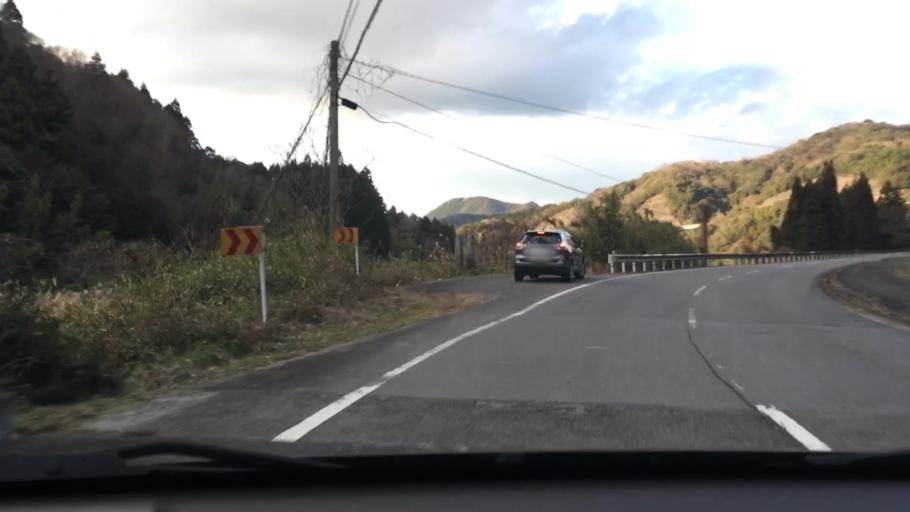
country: JP
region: Oita
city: Hiji
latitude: 33.4263
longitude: 131.4137
